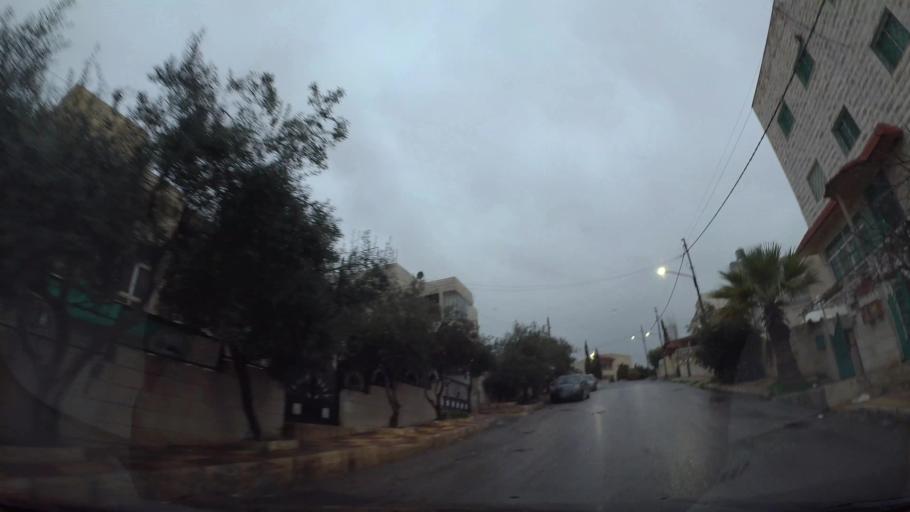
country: JO
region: Amman
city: Amman
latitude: 32.0010
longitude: 35.9661
